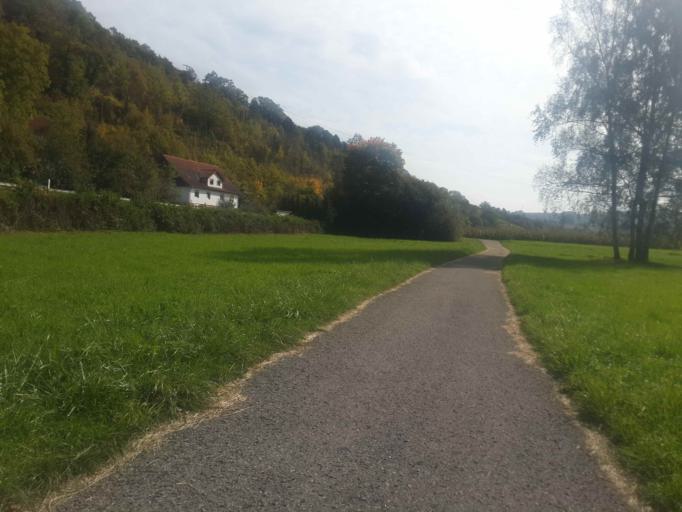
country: DE
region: Baden-Wuerttemberg
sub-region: Regierungsbezirk Stuttgart
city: Neudenau
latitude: 49.3031
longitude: 9.3114
